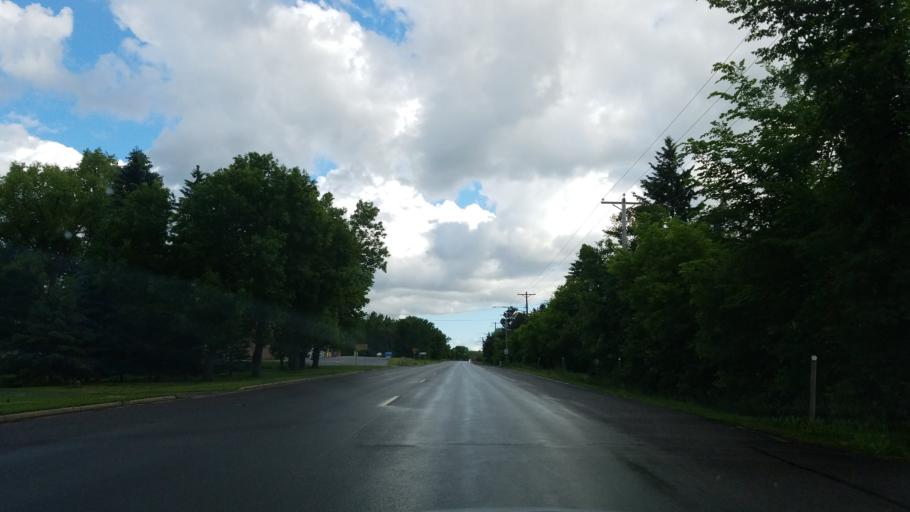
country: US
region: Wisconsin
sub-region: Polk County
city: Saint Croix Falls
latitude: 45.3540
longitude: -92.6374
